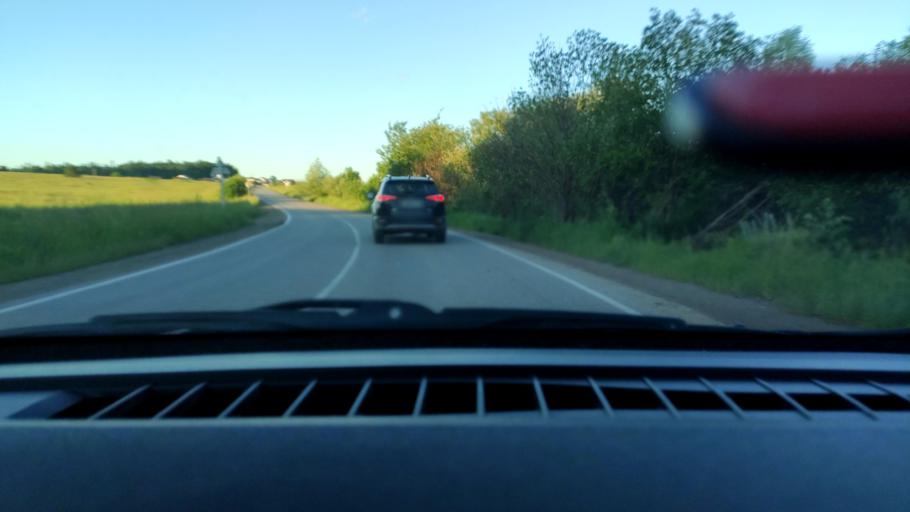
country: RU
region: Perm
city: Kultayevo
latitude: 57.9183
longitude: 55.9317
